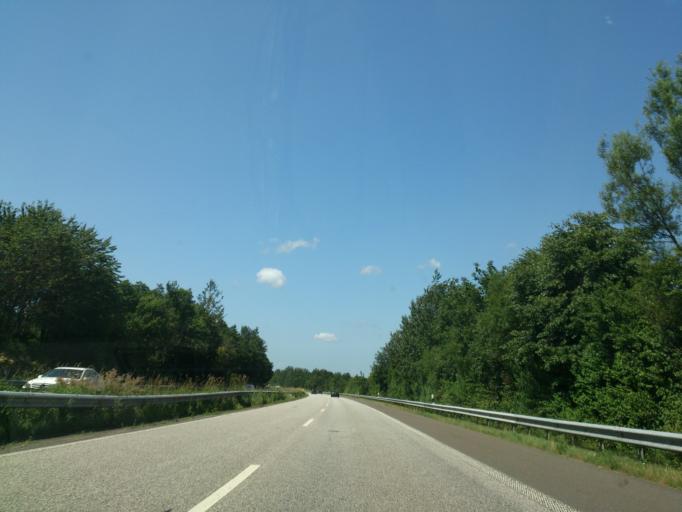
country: DE
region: Schleswig-Holstein
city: Nordhastedt
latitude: 54.1626
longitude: 9.2067
